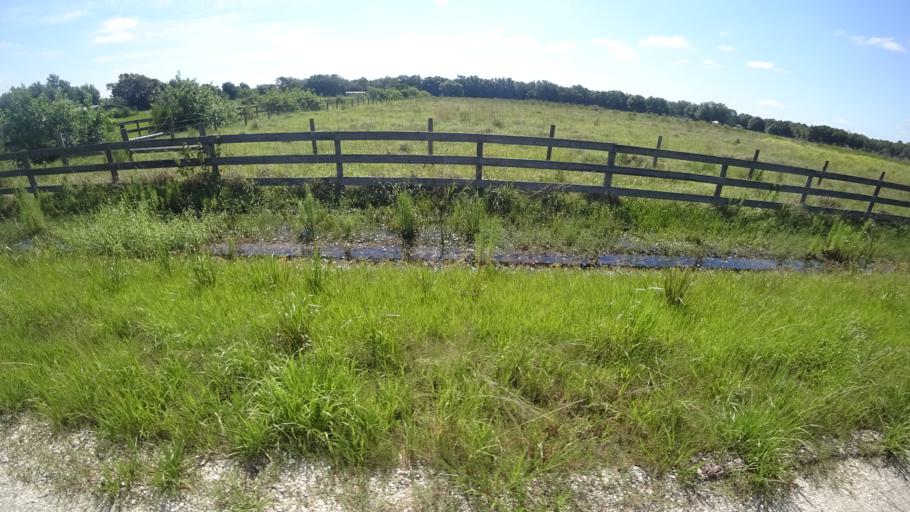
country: US
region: Florida
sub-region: Sarasota County
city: The Meadows
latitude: 27.4374
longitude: -82.3201
